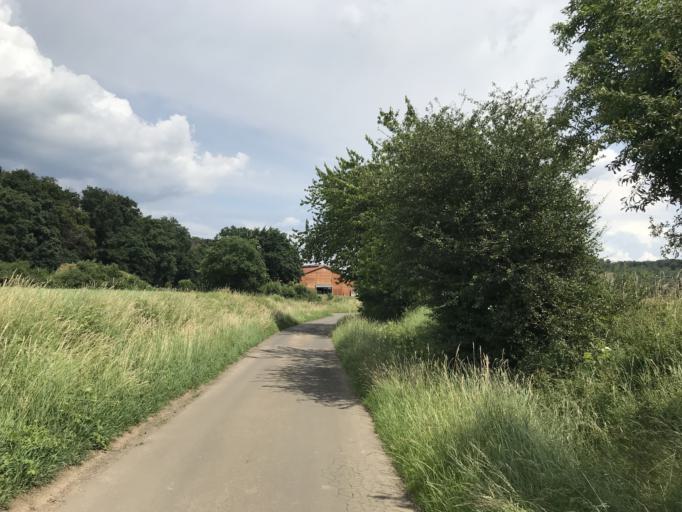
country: DE
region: Hesse
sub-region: Regierungsbezirk Giessen
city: Hungen
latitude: 50.4699
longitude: 8.9328
